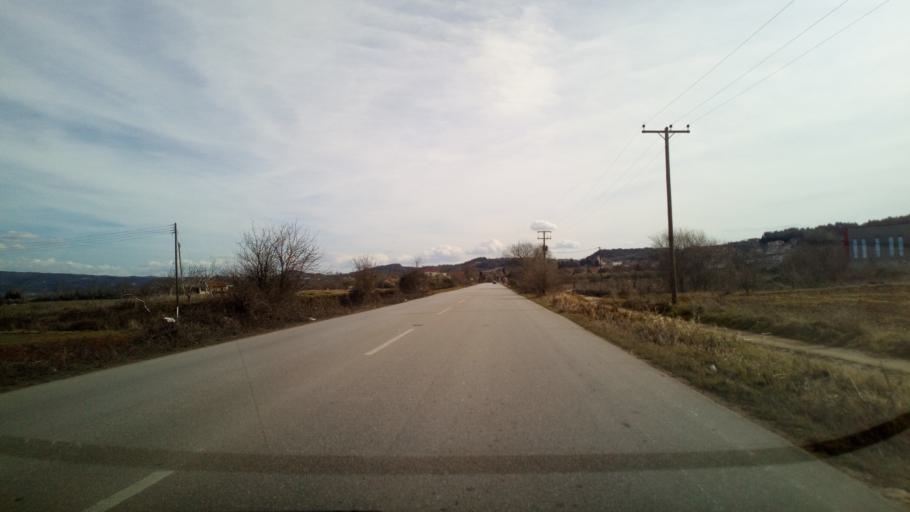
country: GR
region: Central Macedonia
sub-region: Nomos Thessalonikis
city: Gerakarou
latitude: 40.6405
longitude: 23.1846
